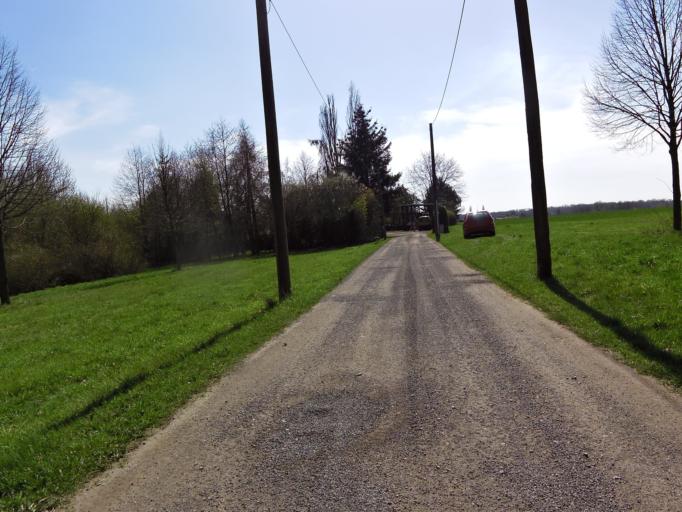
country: DE
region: Saxony
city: Schkeuditz
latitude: 51.3863
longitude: 12.2901
